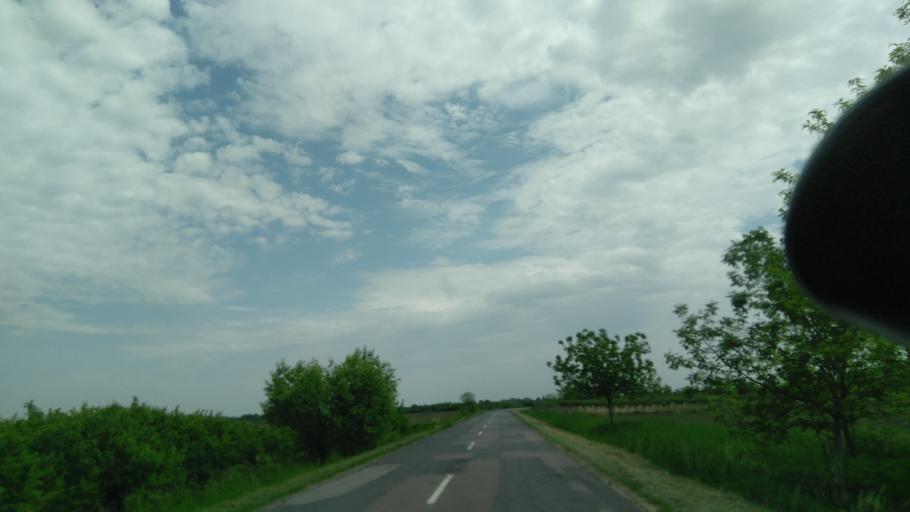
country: HU
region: Hajdu-Bihar
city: Komadi
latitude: 47.0234
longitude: 21.5716
